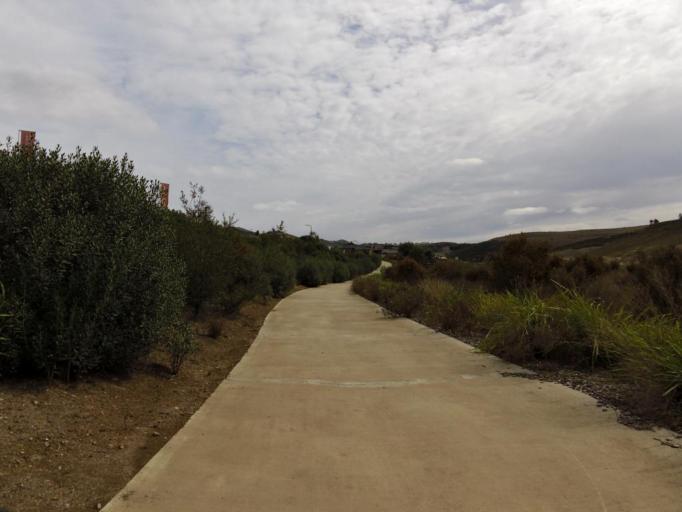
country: AU
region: Victoria
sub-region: Hume
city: Sunbury
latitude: -37.5621
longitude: 144.6994
